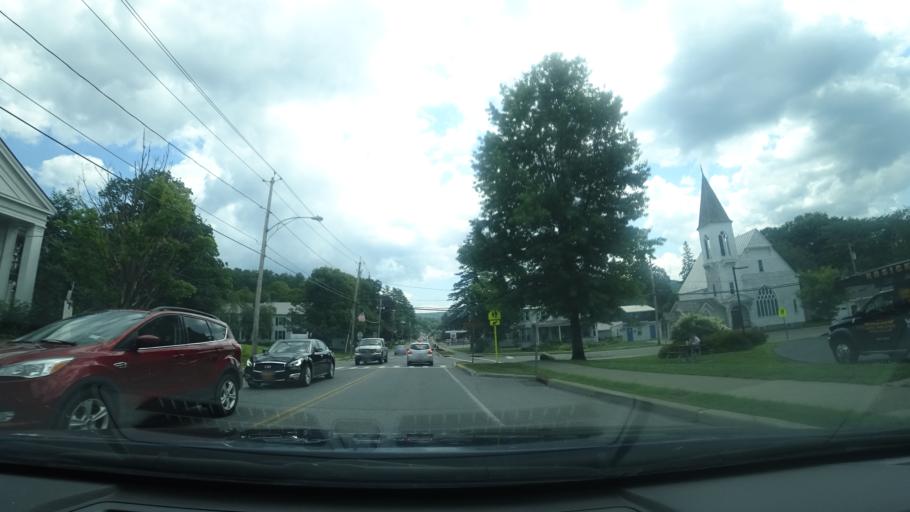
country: US
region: New York
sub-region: Warren County
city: Warrensburg
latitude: 43.4951
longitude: -73.7729
